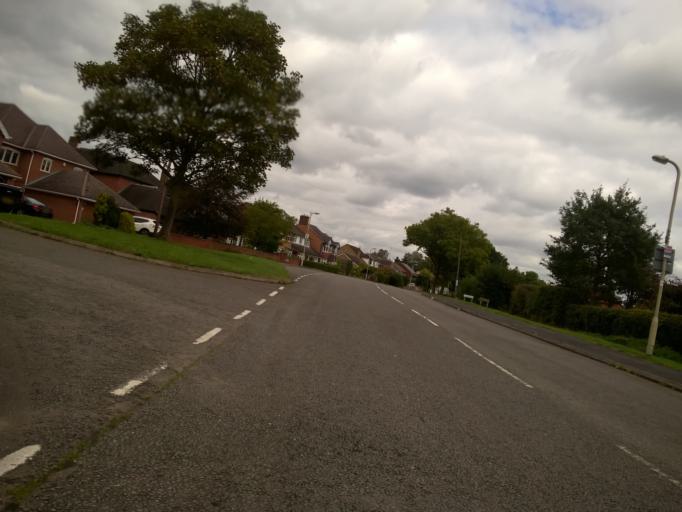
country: GB
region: England
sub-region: Leicestershire
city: Kirby Muxloe
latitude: 52.6393
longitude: -1.2264
